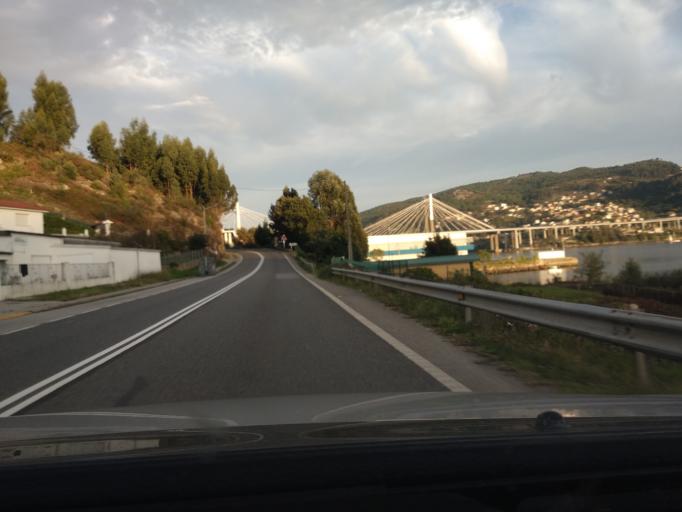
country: ES
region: Galicia
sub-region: Provincia de Pontevedra
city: Redondela
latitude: 42.2915
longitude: -8.6729
